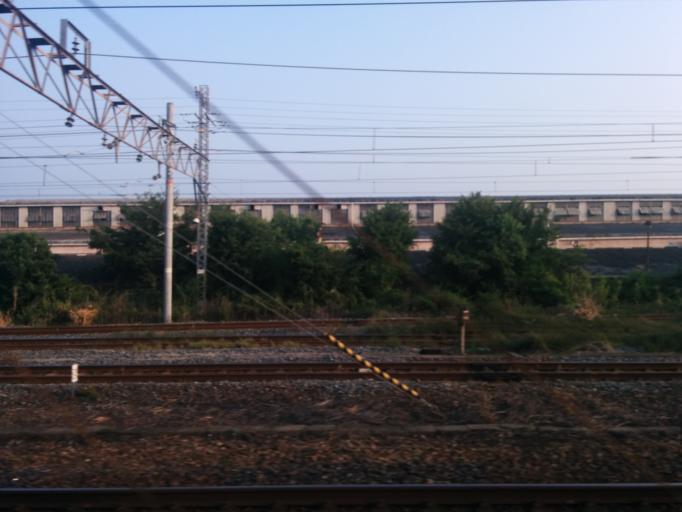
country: JP
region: Kyoto
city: Muko
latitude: 34.9802
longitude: 135.7298
